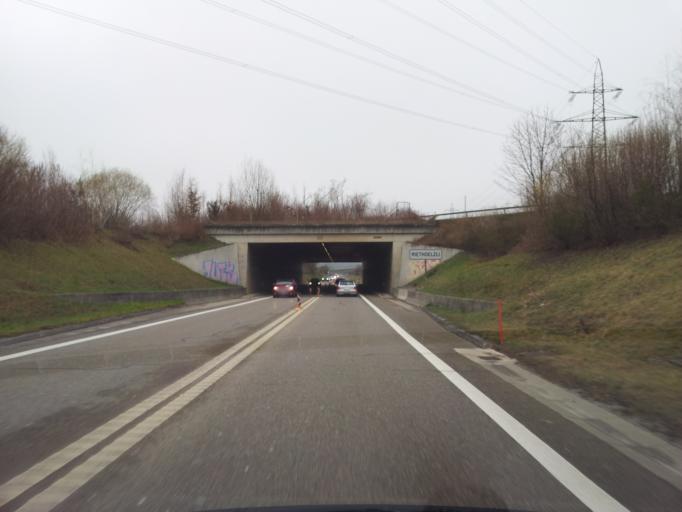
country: CH
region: Zurich
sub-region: Bezirk Winterthur
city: Hettlingen
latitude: 47.5345
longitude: 8.6928
